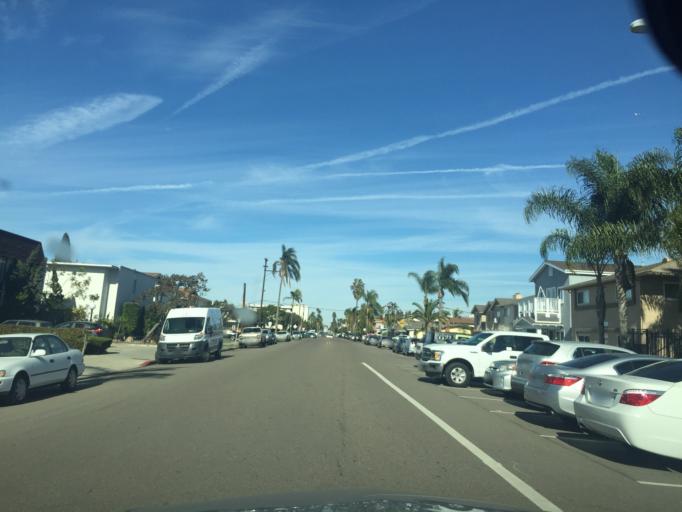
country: US
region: California
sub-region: San Diego County
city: San Diego
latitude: 32.7511
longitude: -117.1289
